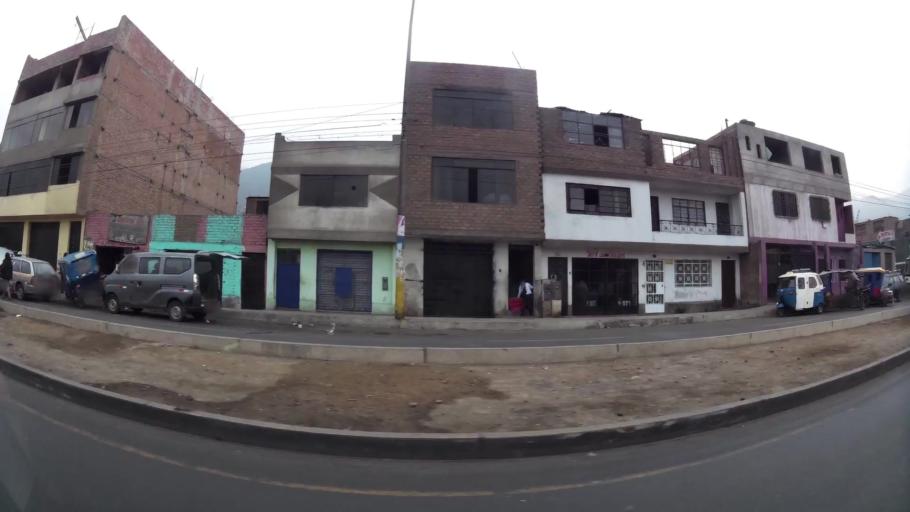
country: PE
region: Lima
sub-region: Lima
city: Independencia
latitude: -11.9877
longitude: -77.0157
